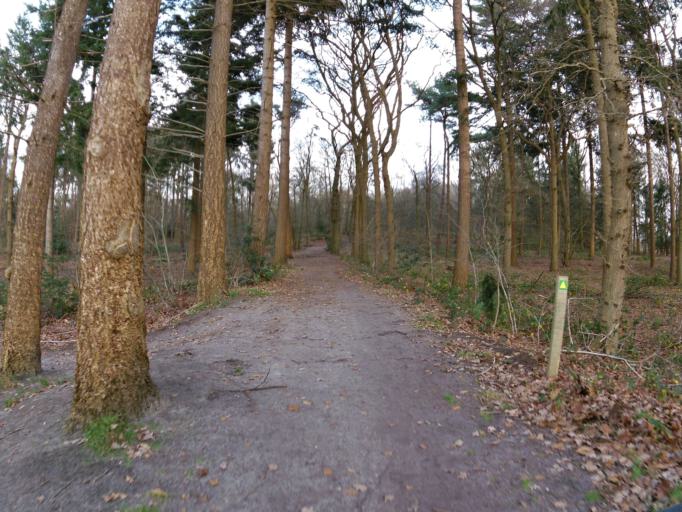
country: NL
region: North Brabant
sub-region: Gemeente Vught
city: Vught
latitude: 51.6648
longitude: 5.3188
